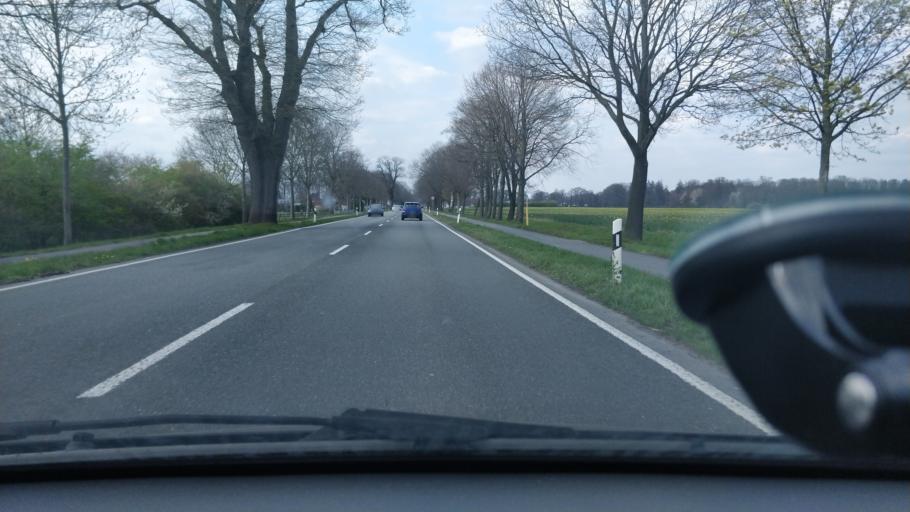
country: DE
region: North Rhine-Westphalia
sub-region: Regierungsbezirk Dusseldorf
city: Hamminkeln
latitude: 51.7018
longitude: 6.6028
